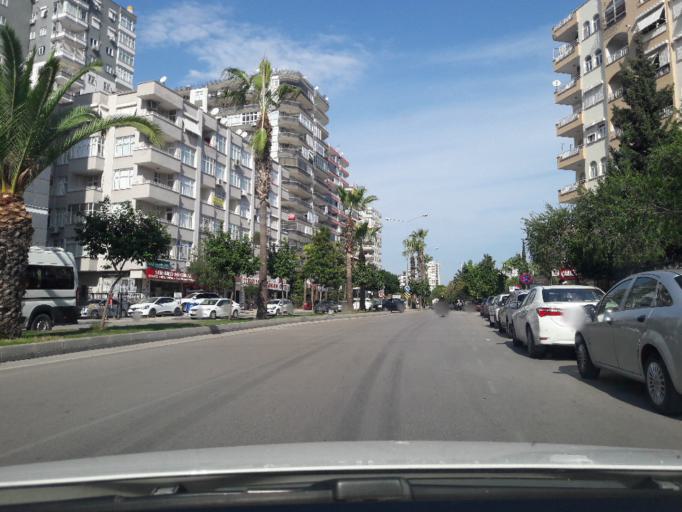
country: TR
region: Adana
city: Adana
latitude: 37.0164
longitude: 35.3221
